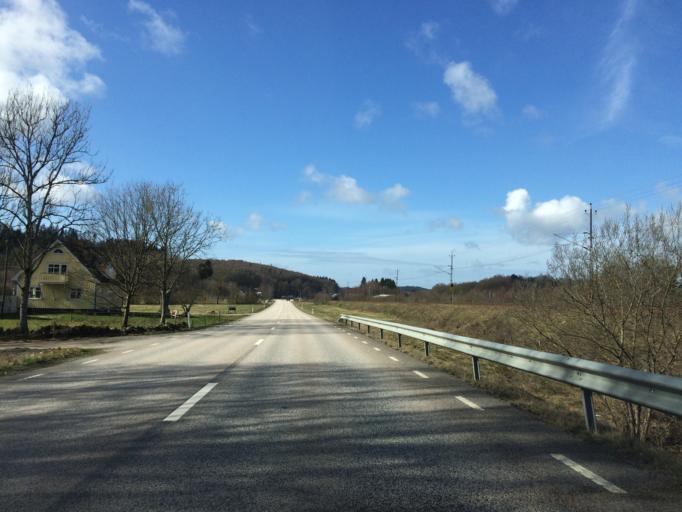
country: SE
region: Halland
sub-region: Laholms Kommun
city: Knared
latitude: 56.5090
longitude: 13.3376
